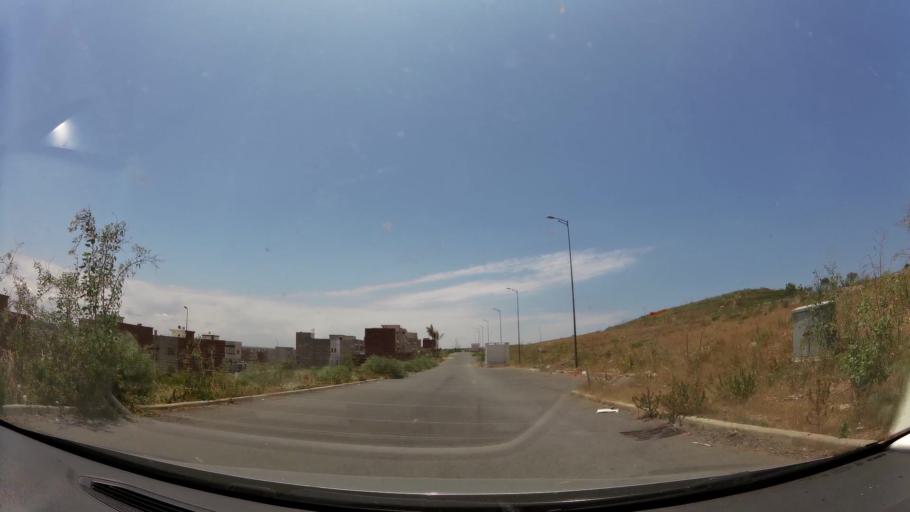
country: MA
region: Gharb-Chrarda-Beni Hssen
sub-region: Kenitra Province
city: Kenitra
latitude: 34.2515
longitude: -6.6591
